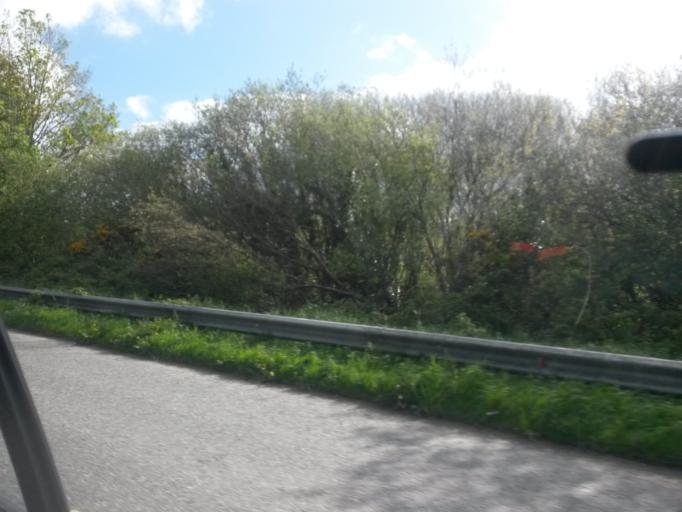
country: IE
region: Leinster
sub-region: Loch Garman
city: Enniscorthy
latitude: 52.5179
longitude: -6.5650
